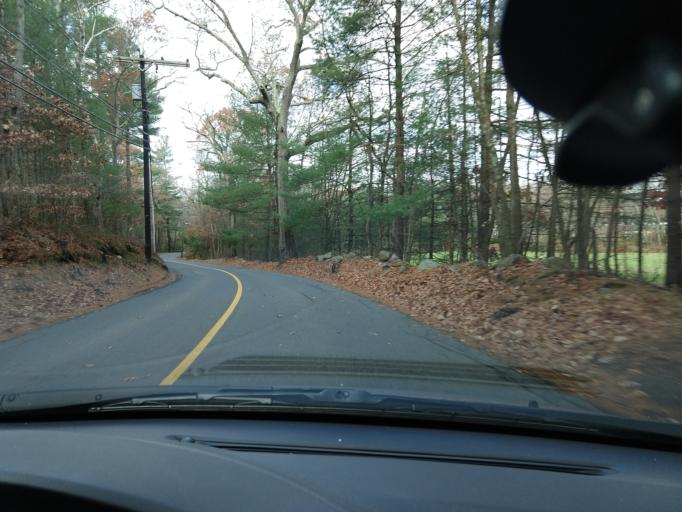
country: US
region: Massachusetts
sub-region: Middlesex County
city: West Concord
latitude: 42.4761
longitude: -71.3797
